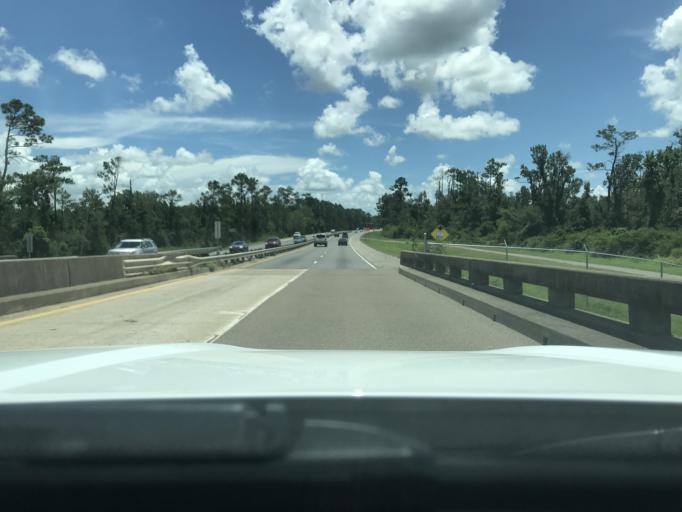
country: US
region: Louisiana
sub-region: Calcasieu Parish
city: Moss Bluff
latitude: 30.2831
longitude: -93.1867
